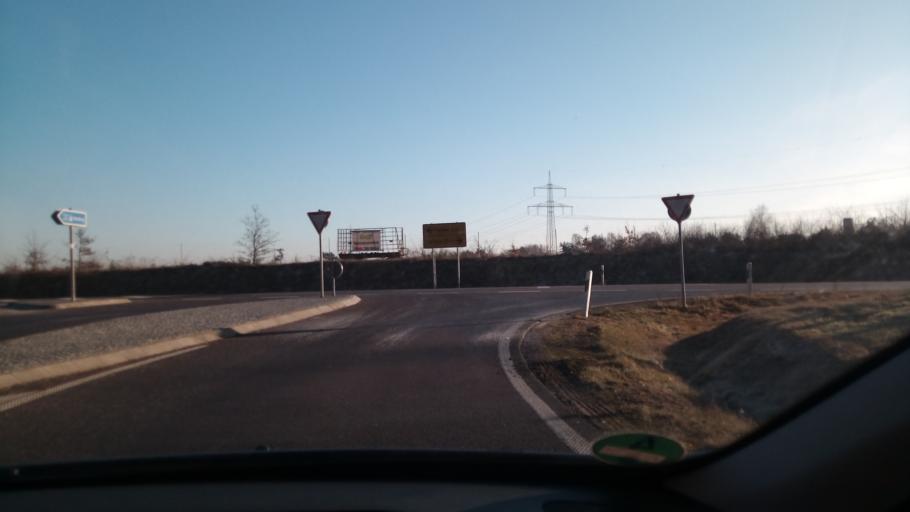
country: DE
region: Schleswig-Holstein
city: Besenthal
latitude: 53.5386
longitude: 10.7315
